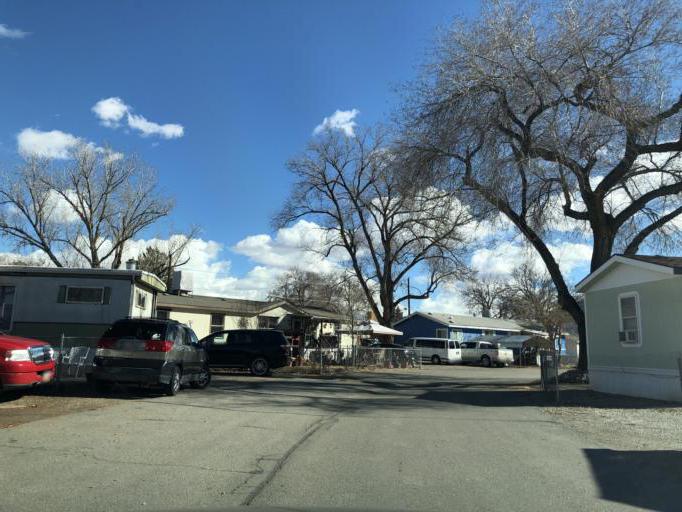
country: US
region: Utah
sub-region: Grand County
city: Moab
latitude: 38.5777
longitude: -109.5622
